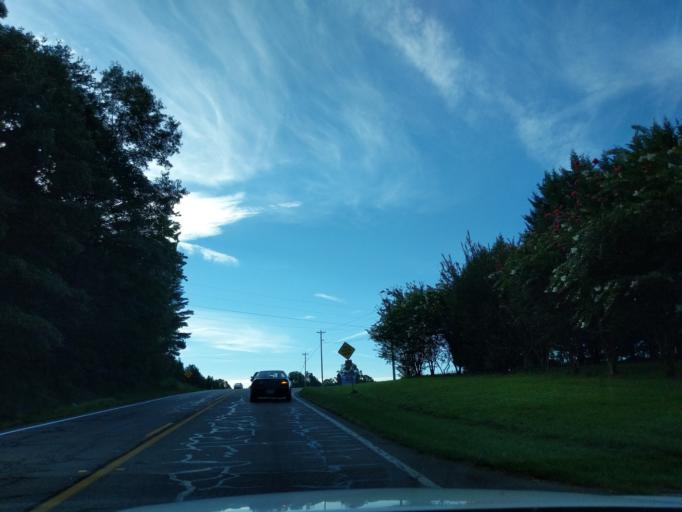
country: US
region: Georgia
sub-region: Fannin County
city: Blue Ridge
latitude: 34.8890
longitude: -84.3448
